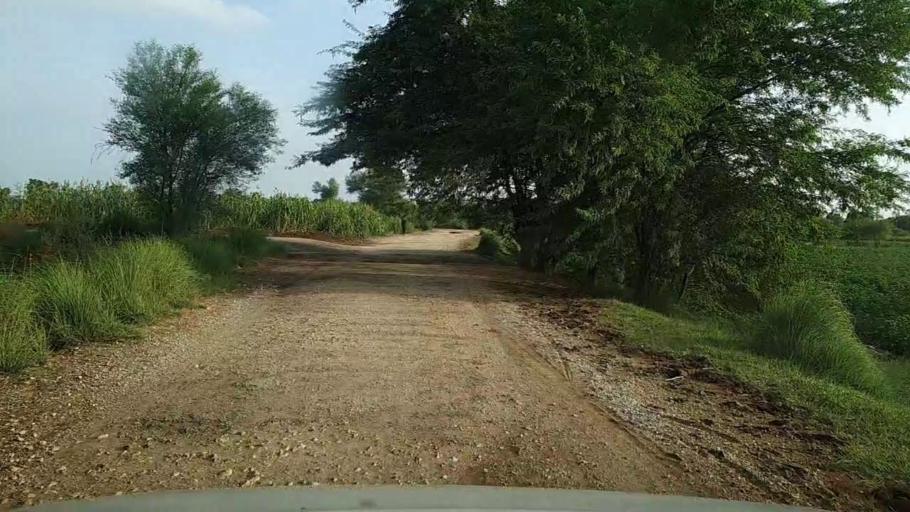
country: PK
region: Sindh
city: Pad Idan
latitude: 26.7836
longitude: 68.2208
